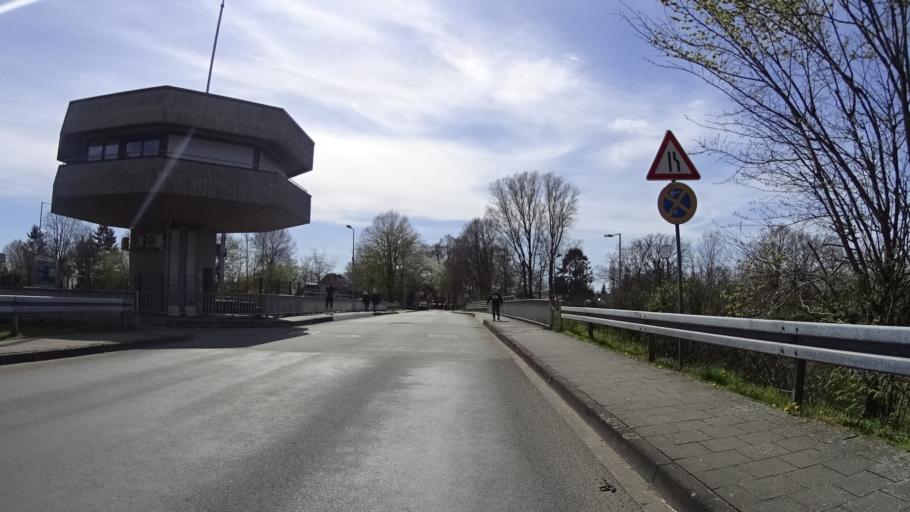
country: DE
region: North Rhine-Westphalia
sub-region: Regierungsbezirk Munster
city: Dreierwalde
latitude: 52.3064
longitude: 7.4748
